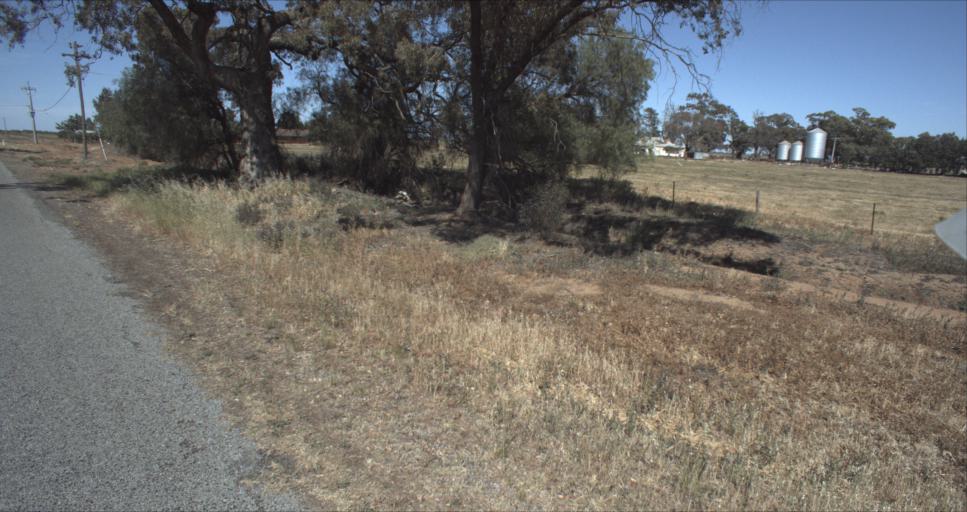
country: AU
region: New South Wales
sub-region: Leeton
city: Leeton
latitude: -34.5432
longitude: 146.3161
